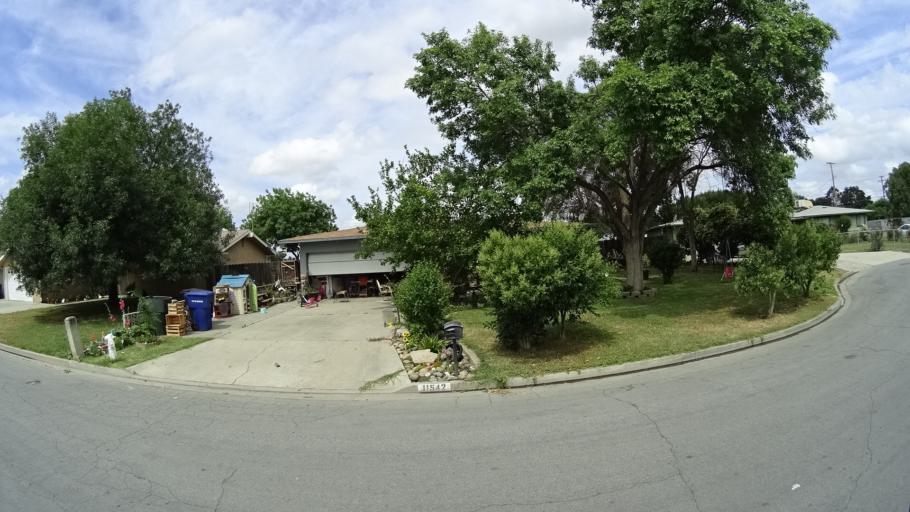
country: US
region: California
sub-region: Kings County
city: Home Garden
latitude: 36.3045
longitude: -119.6609
